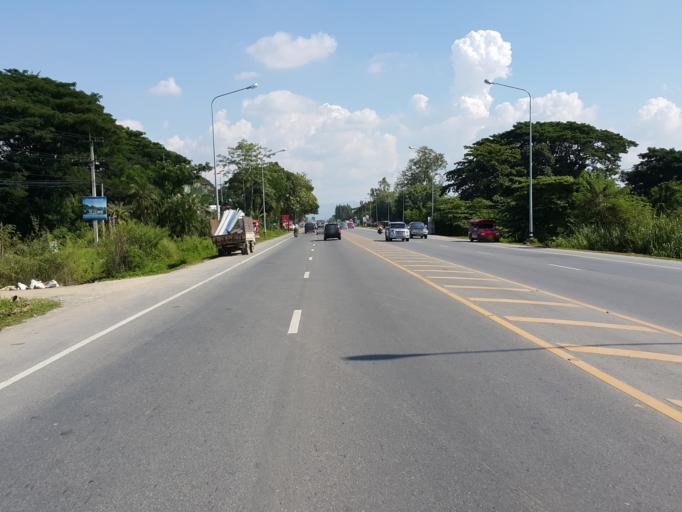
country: TH
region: Chiang Mai
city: Saraphi
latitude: 18.7595
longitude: 99.0454
